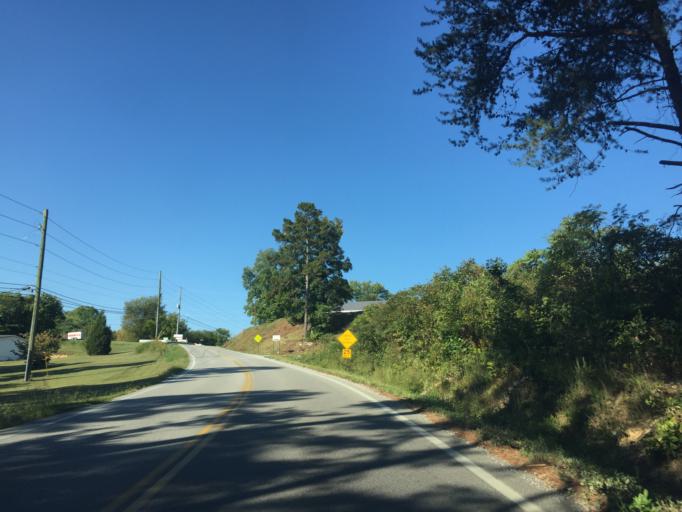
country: US
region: Tennessee
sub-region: Hamilton County
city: Harrison
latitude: 35.1215
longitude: -85.1056
